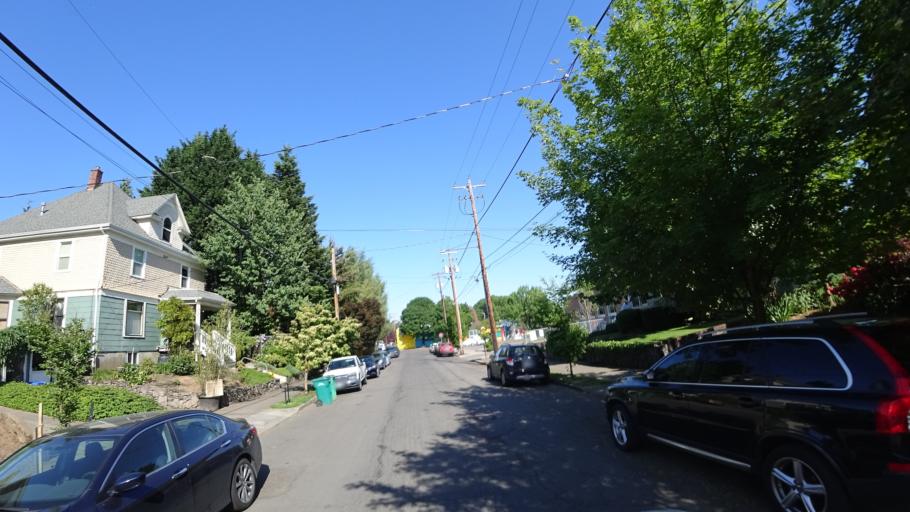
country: US
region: Oregon
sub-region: Multnomah County
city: Portland
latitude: 45.5429
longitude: -122.6627
